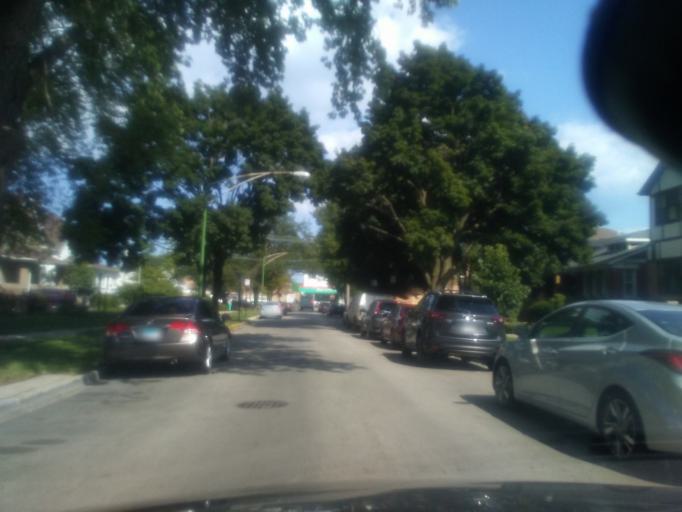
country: US
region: Illinois
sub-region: Cook County
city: Lincolnwood
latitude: 41.9589
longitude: -87.7490
